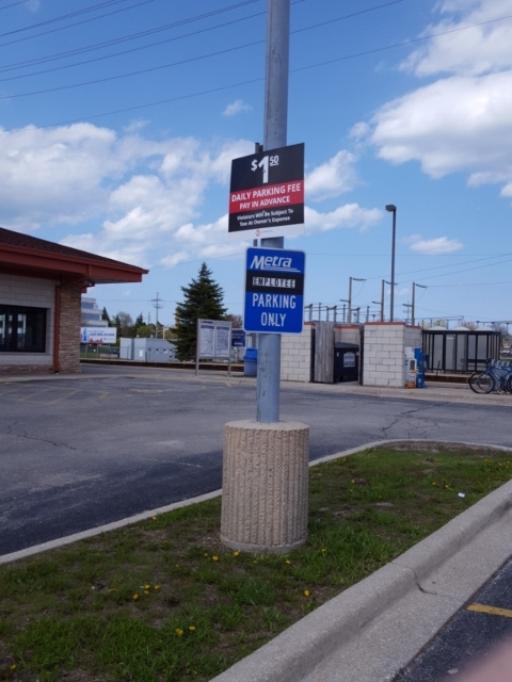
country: US
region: Illinois
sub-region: Lake County
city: Deerfield
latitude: 42.1515
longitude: -87.8412
